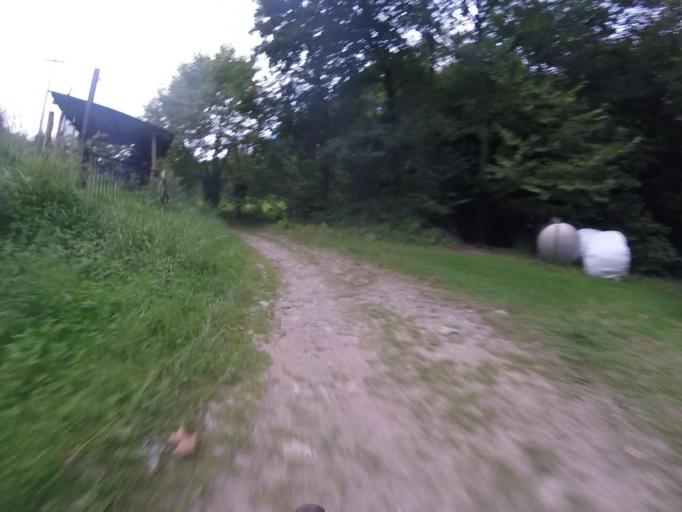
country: ES
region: Basque Country
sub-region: Provincia de Guipuzcoa
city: Errenteria
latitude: 43.2780
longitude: -1.8472
